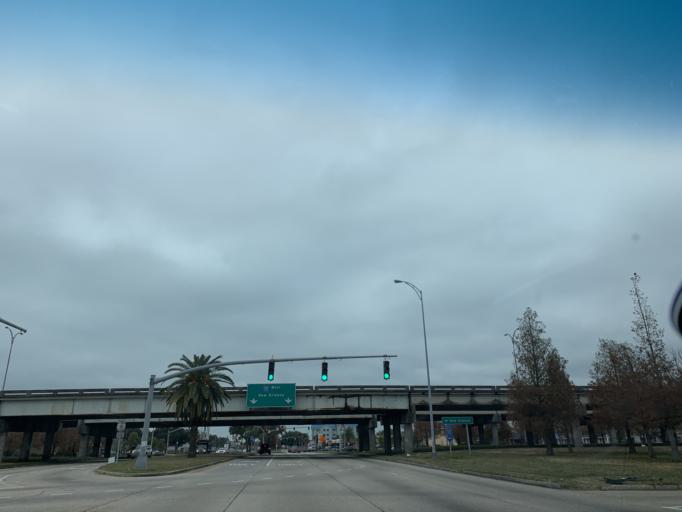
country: US
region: Louisiana
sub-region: Saint Bernard Parish
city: Arabi
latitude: 30.0457
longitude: -89.9606
